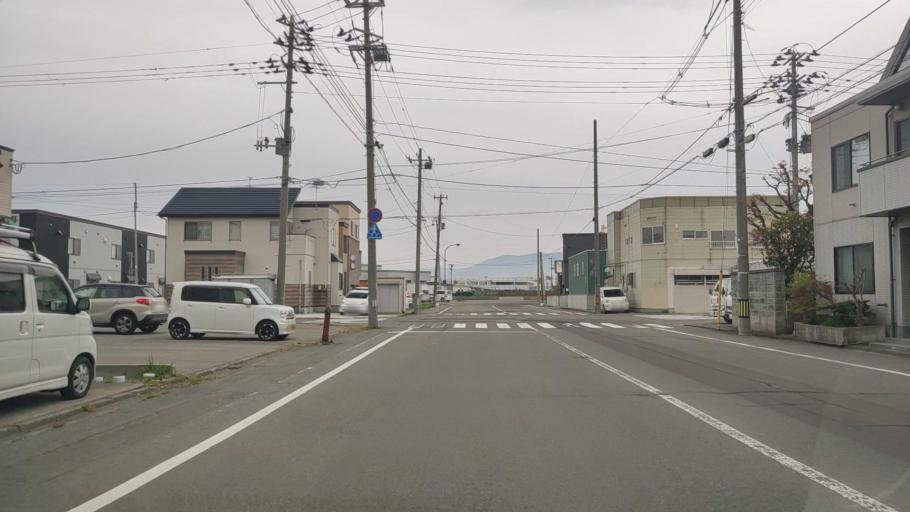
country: JP
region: Aomori
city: Aomori Shi
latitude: 40.8294
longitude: 140.7585
